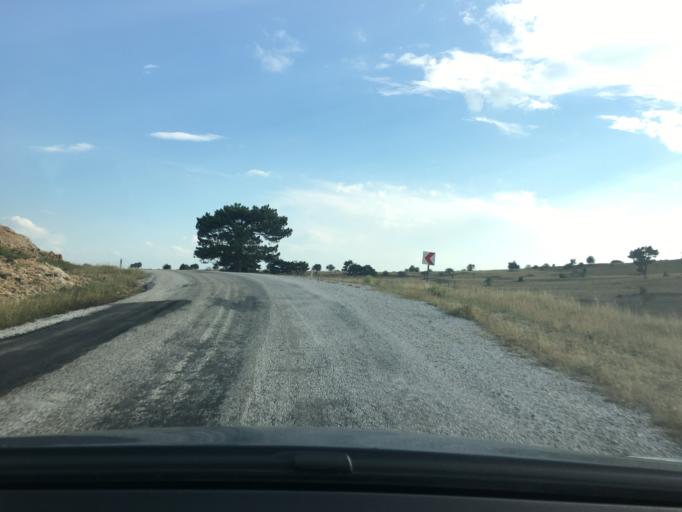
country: TR
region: Eskisehir
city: Kirka
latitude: 39.2837
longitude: 30.6737
